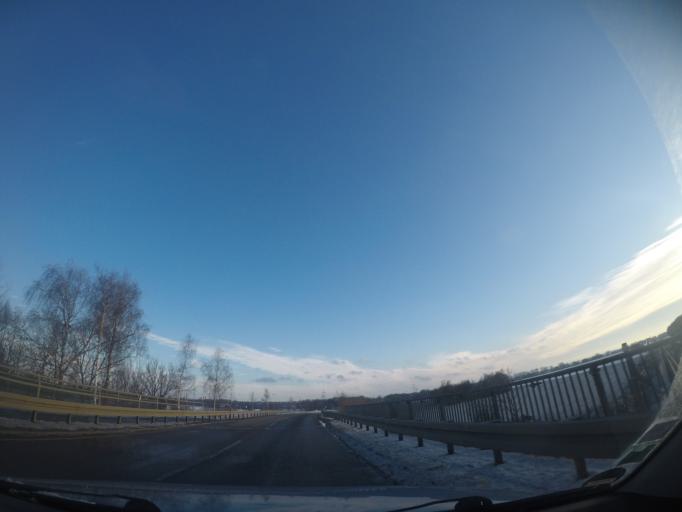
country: DE
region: Baden-Wuerttemberg
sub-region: Tuebingen Region
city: Laupheim
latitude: 48.2492
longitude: 9.8567
